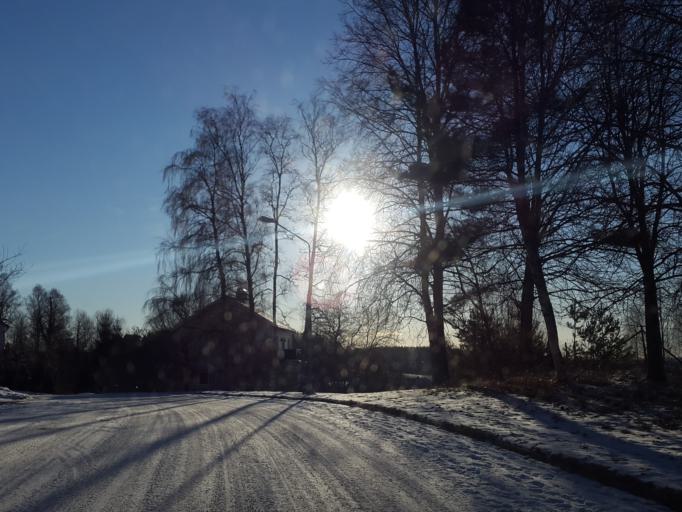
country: SE
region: Vaestra Goetaland
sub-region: Vargarda Kommun
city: Vargarda
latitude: 58.0285
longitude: 12.8015
